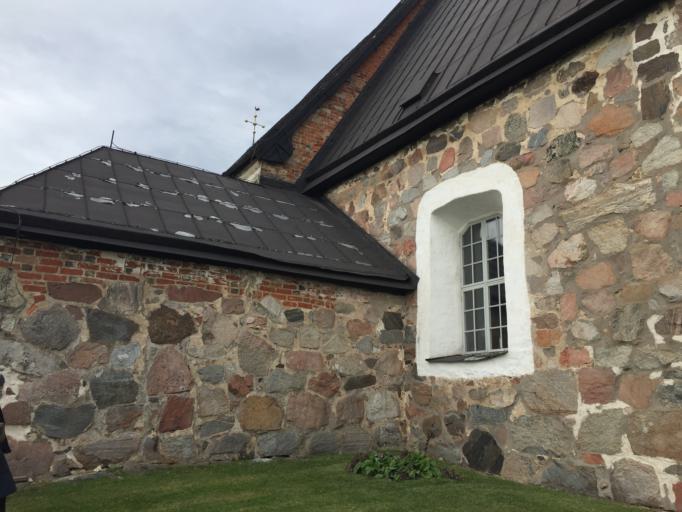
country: SE
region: Stockholm
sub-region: Norrtalje Kommun
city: Rimbo
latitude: 59.7330
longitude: 18.5021
